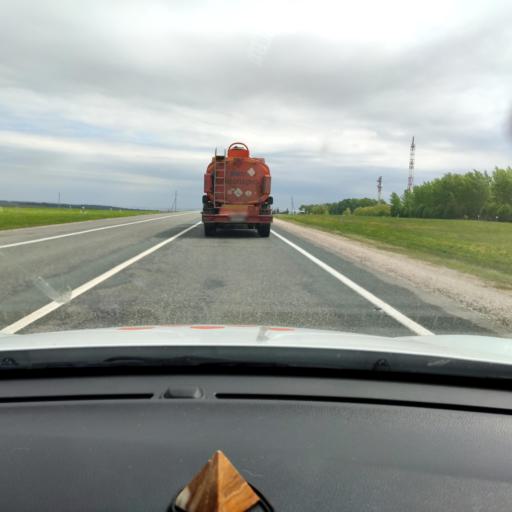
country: RU
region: Tatarstan
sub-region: Alekseyevskiy Rayon
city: Alekseyevskoye
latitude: 55.3824
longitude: 49.9193
